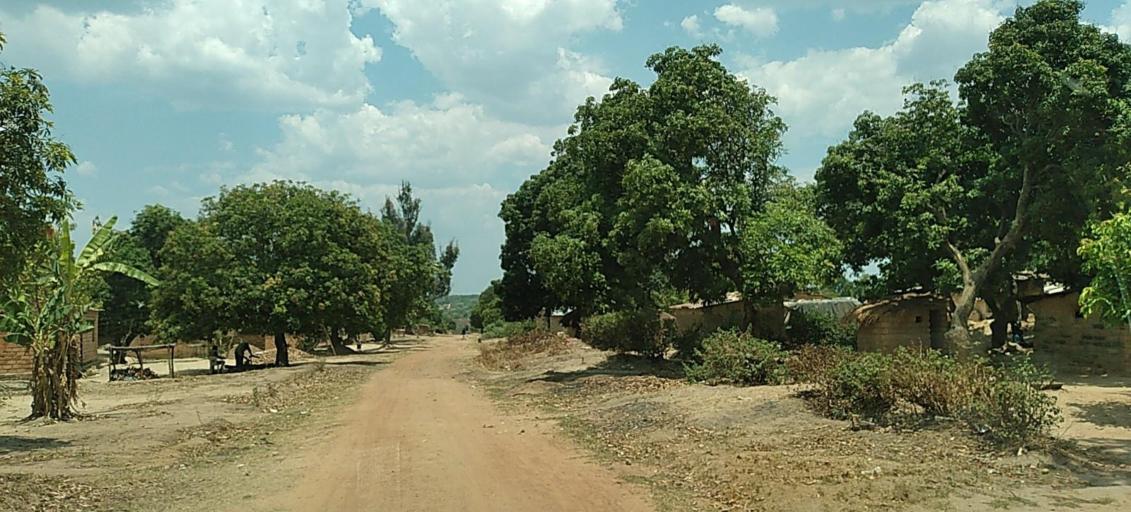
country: ZM
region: Copperbelt
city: Luanshya
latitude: -13.3685
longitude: 28.4112
